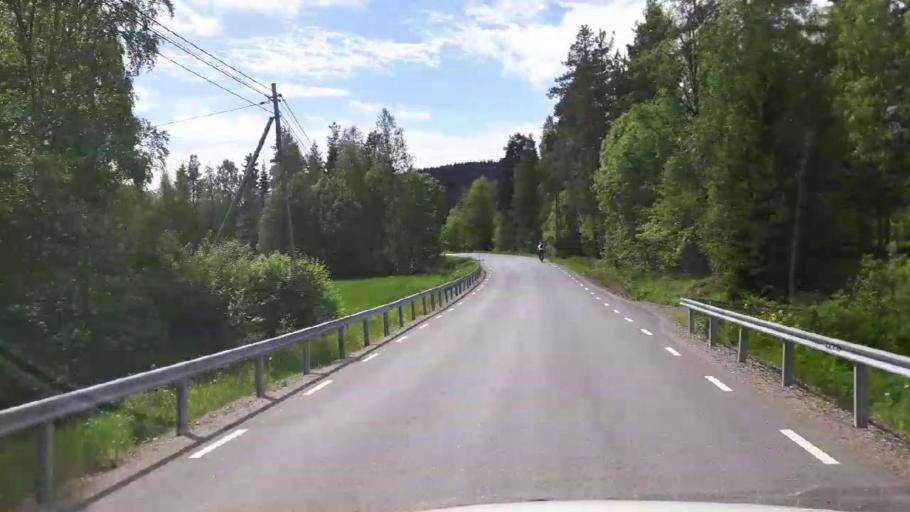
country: SE
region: Dalarna
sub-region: Faluns Kommun
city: Falun
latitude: 60.6731
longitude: 15.7516
